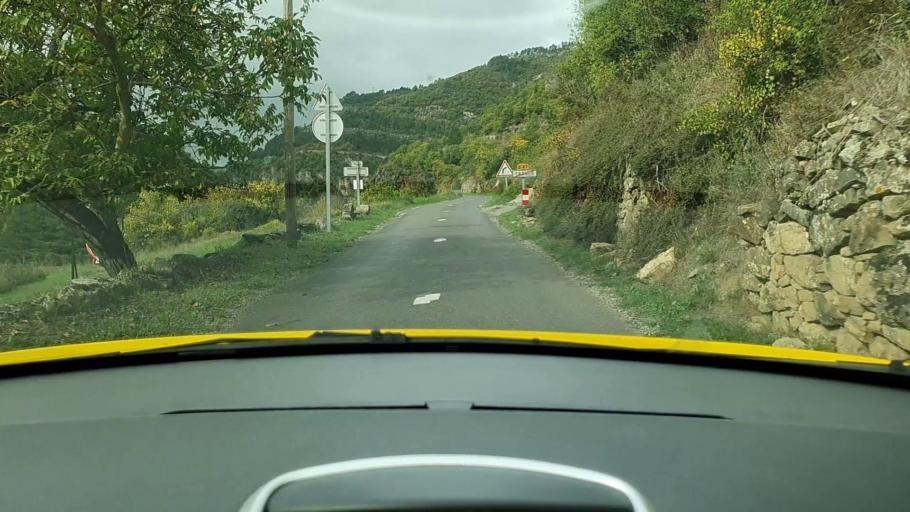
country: FR
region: Languedoc-Roussillon
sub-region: Departement de la Lozere
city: Meyrueis
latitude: 44.0787
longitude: 3.3874
